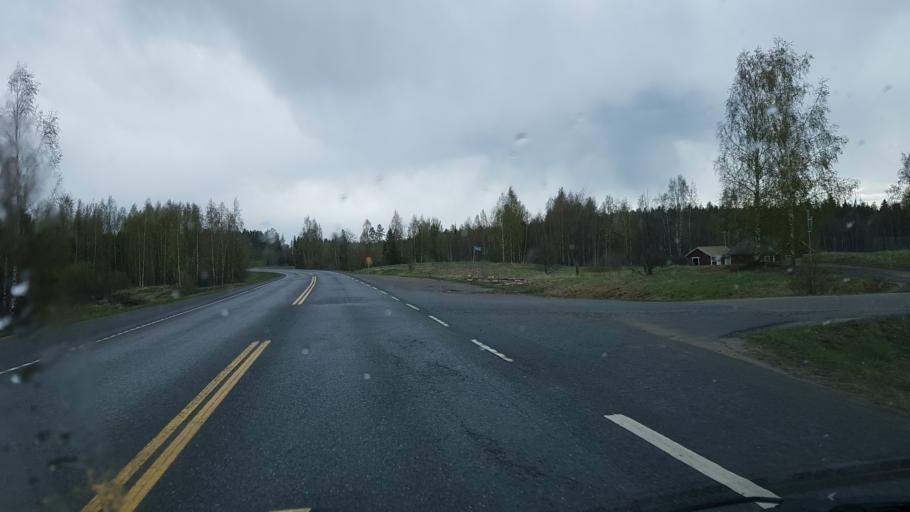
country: FI
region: Pirkanmaa
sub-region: Tampere
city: Pirkkala
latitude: 61.4229
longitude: 23.6346
